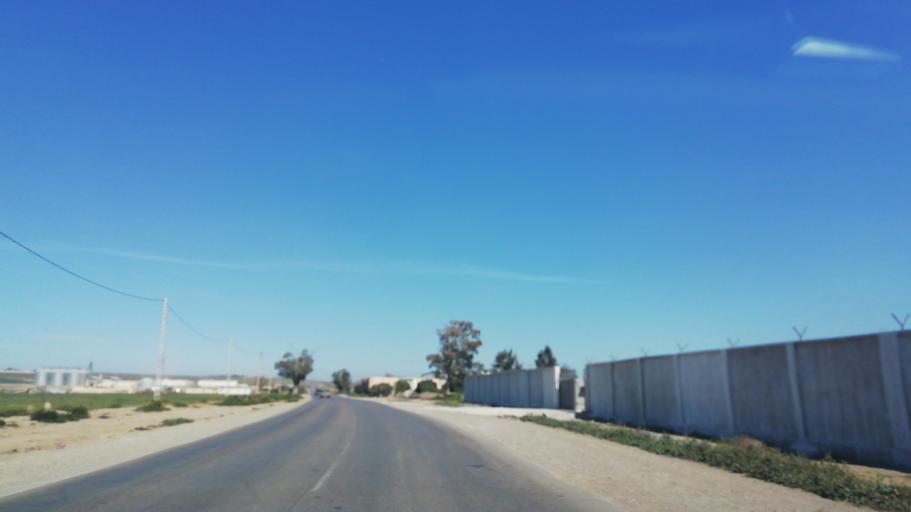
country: DZ
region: Oran
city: Es Senia
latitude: 35.5133
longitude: -0.5898
